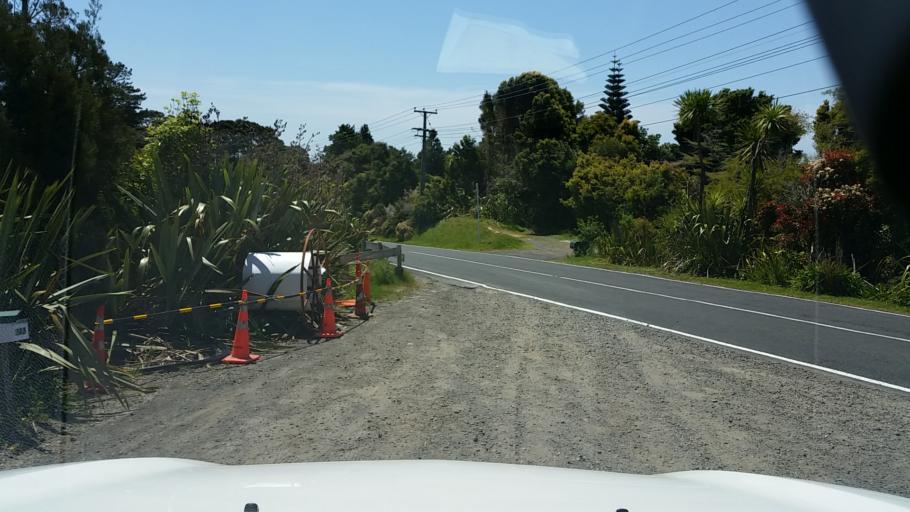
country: NZ
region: Auckland
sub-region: Auckland
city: Titirangi
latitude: -36.9259
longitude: 174.5825
